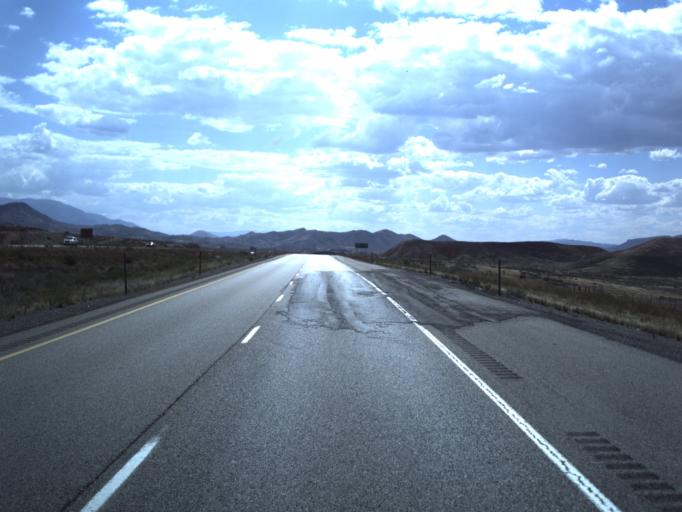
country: US
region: Utah
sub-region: Sevier County
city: Salina
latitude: 38.9284
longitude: -111.8699
